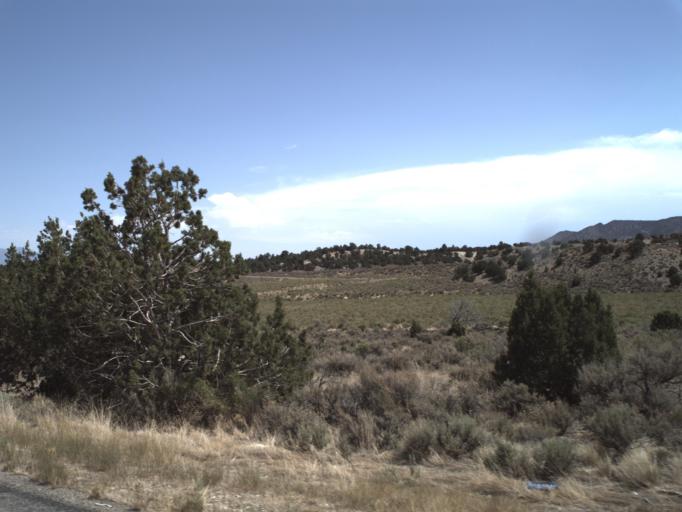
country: US
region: Utah
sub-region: Utah County
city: Eagle Mountain
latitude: 40.0094
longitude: -112.2763
